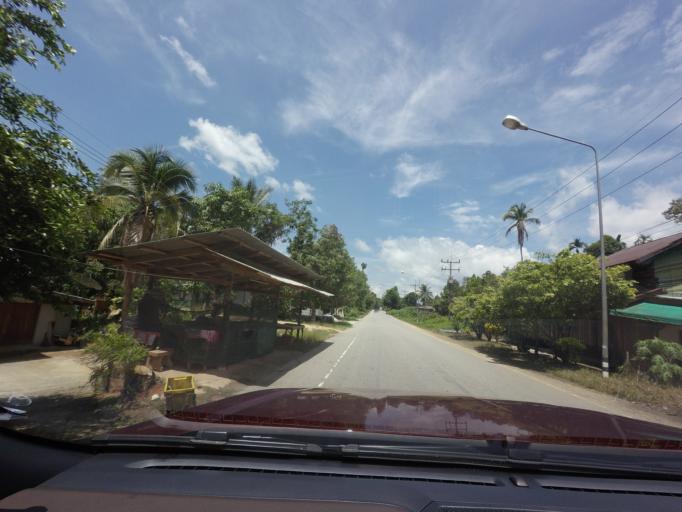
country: TH
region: Narathiwat
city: Ra-ngae
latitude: 6.2505
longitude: 101.6846
